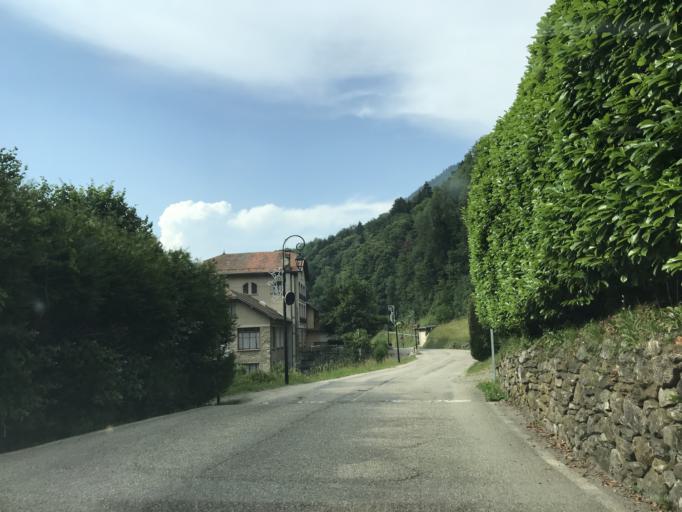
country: FR
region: Rhone-Alpes
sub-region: Departement de l'Isere
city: Allevard
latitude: 45.3577
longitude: 6.0994
